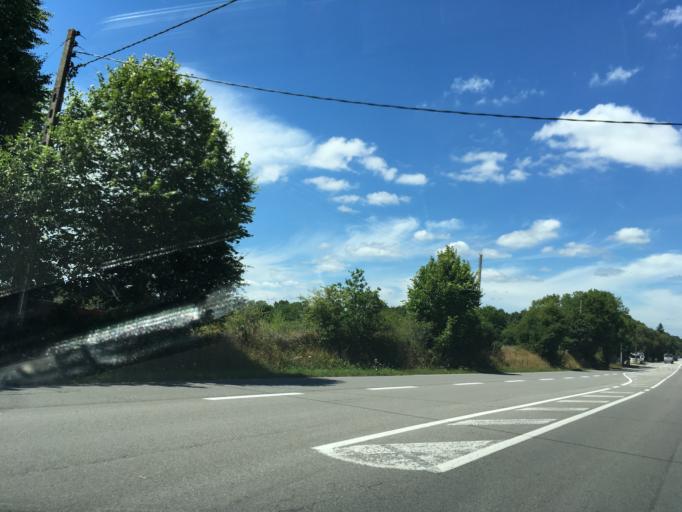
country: FR
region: Brittany
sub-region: Departement du Finistere
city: Quimper
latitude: 47.9515
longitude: -4.0764
